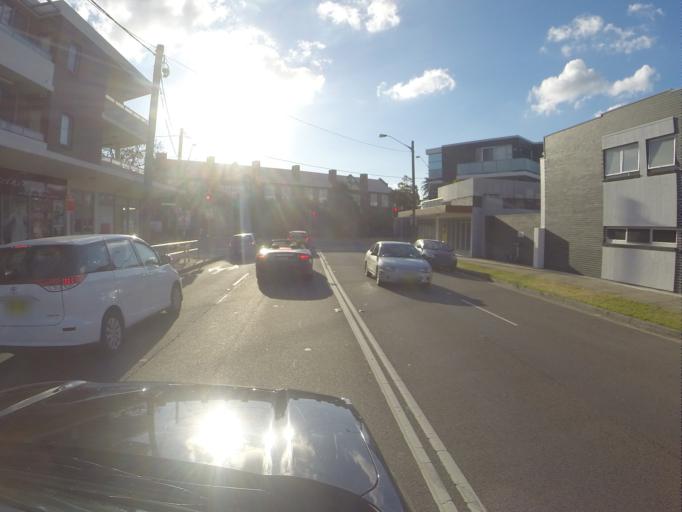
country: AU
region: New South Wales
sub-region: Rockdale
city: Bexley
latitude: -33.9652
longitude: 151.1116
